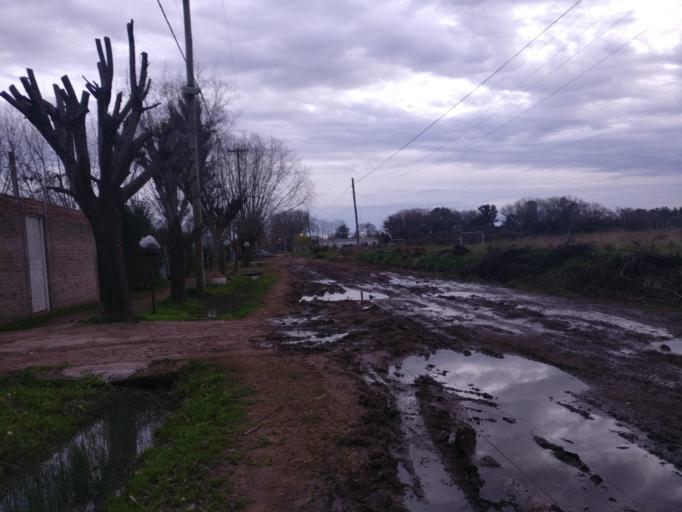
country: AR
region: Buenos Aires
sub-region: Partido de Ezeiza
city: Ezeiza
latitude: -34.9370
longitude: -58.6084
